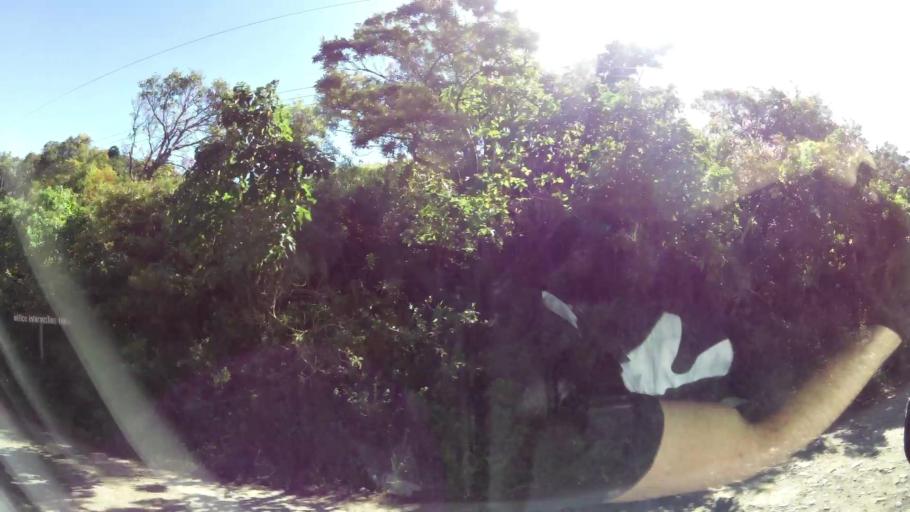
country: CR
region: Guanacaste
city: Juntas
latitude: 10.3282
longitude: -84.8562
